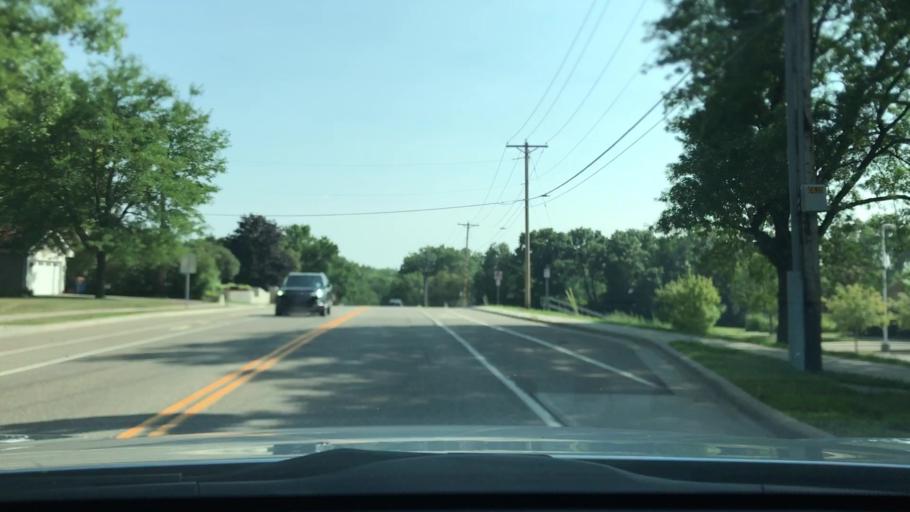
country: US
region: Minnesota
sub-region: Hennepin County
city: Edina
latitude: 44.8969
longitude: -93.3680
